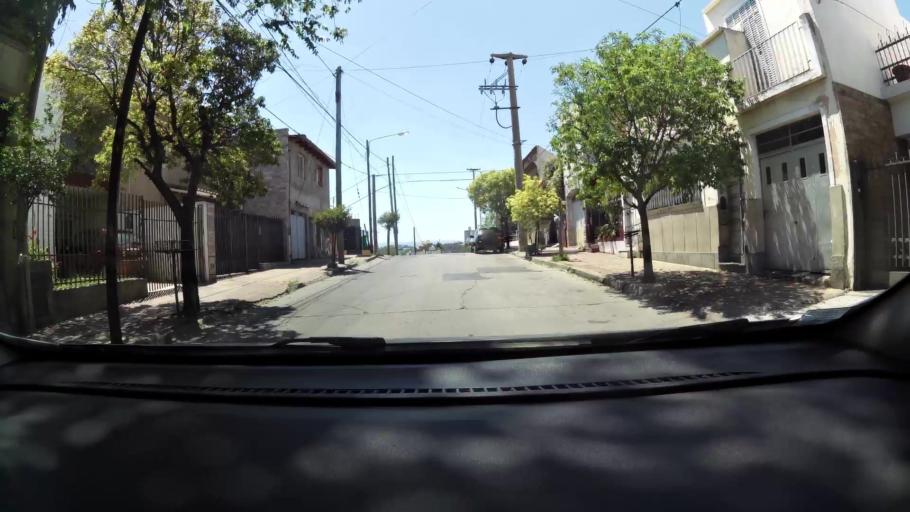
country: AR
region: Cordoba
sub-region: Departamento de Capital
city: Cordoba
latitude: -31.3951
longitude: -64.1990
